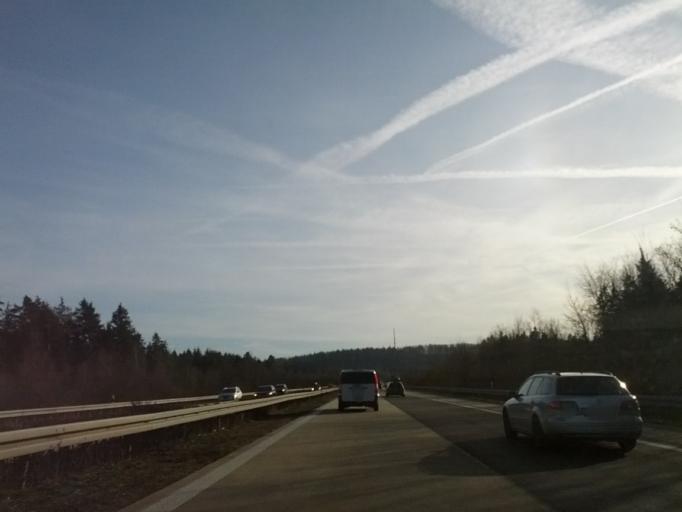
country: DE
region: Baden-Wuerttemberg
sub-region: Regierungsbezirk Stuttgart
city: Ellenberg
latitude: 49.0345
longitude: 10.1889
